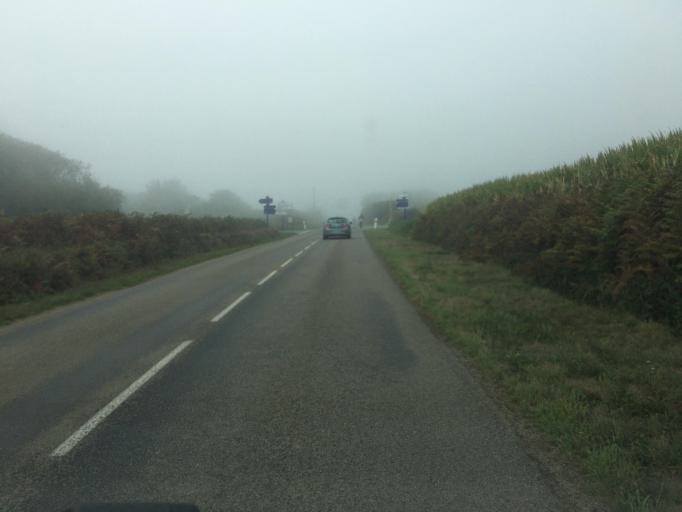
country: FR
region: Brittany
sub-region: Departement du Finistere
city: Plogoff
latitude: 48.0602
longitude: -4.6580
